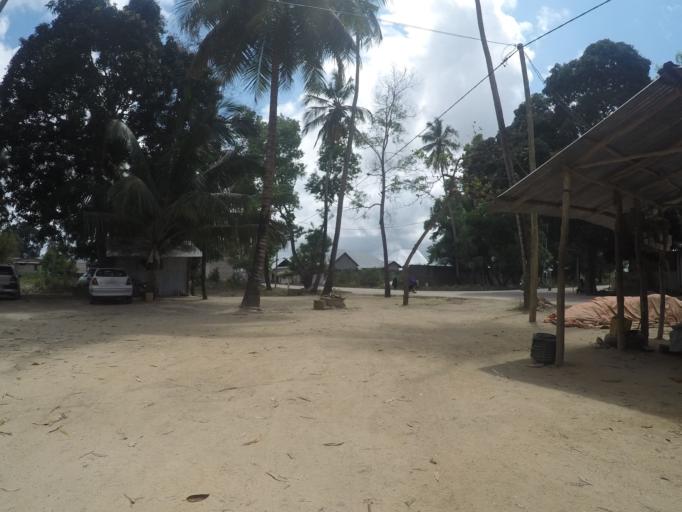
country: TZ
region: Zanzibar Urban/West
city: Zanzibar
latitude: -6.2049
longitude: 39.2431
